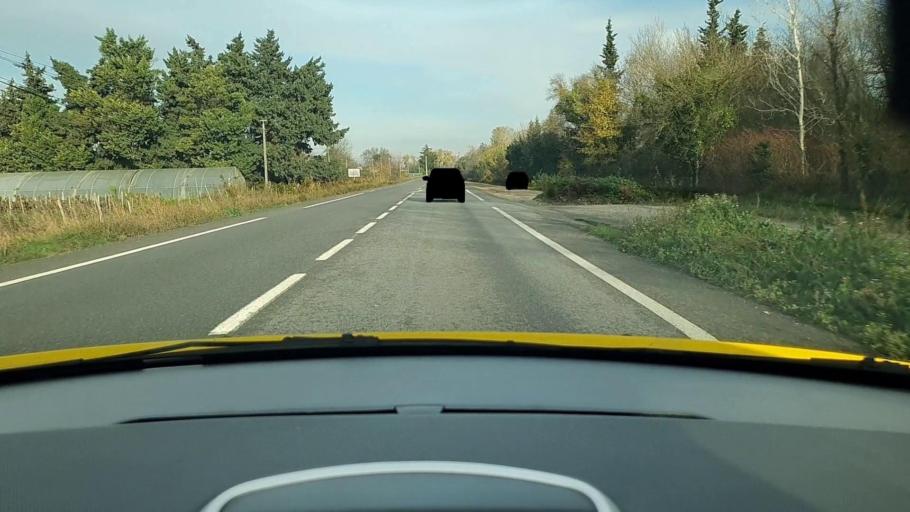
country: FR
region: Languedoc-Roussillon
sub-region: Departement du Gard
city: Fourques
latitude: 43.7103
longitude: 4.6071
